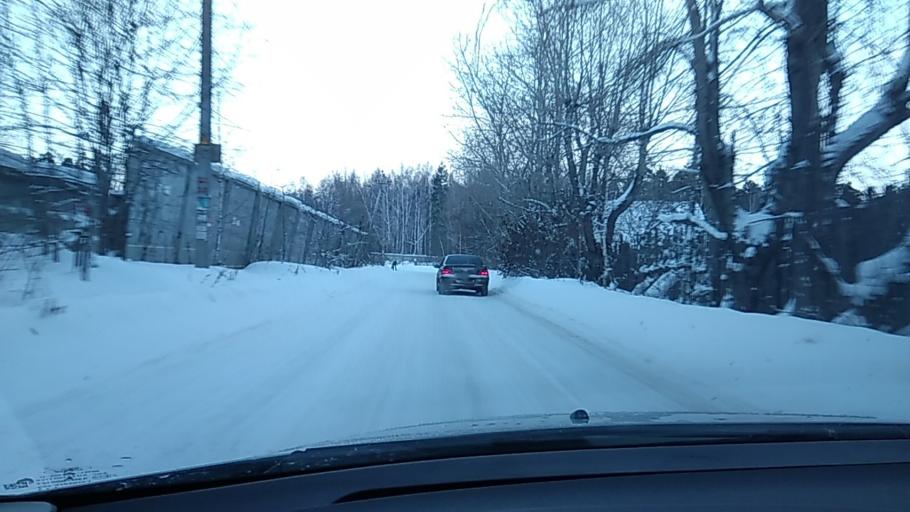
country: RU
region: Sverdlovsk
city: Verkhnyaya Pyshma
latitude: 56.9151
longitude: 60.5817
